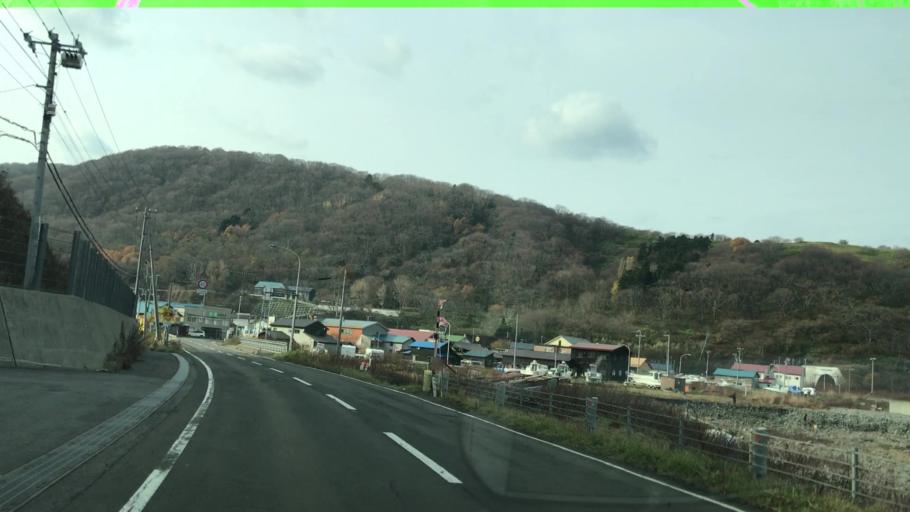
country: JP
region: Hokkaido
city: Iwanai
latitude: 43.3292
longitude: 140.3820
